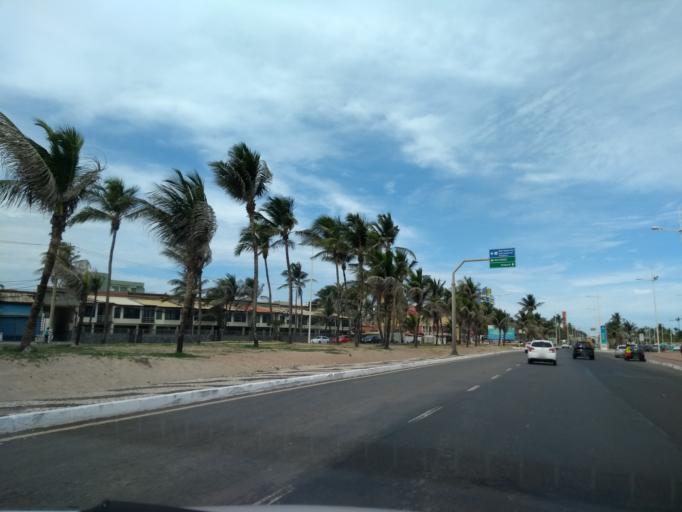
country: BR
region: Bahia
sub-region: Lauro De Freitas
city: Lauro de Freitas
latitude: -12.9549
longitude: -38.3845
